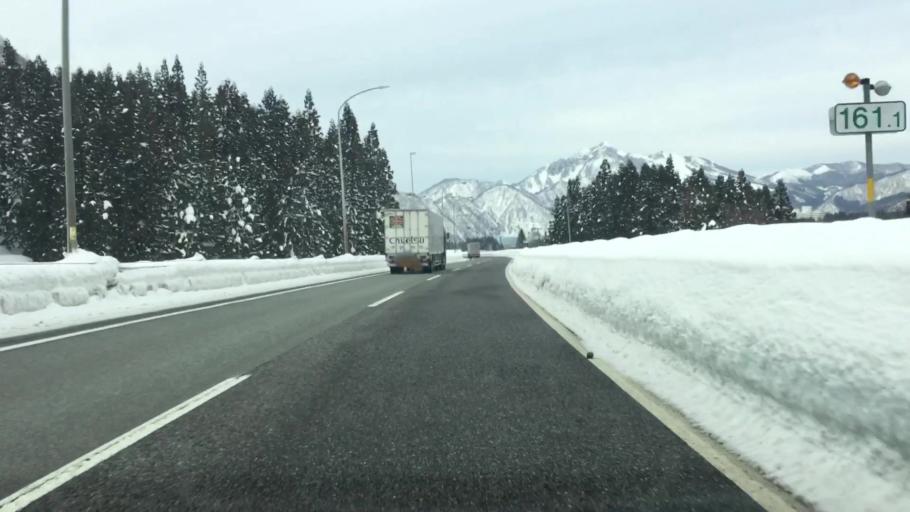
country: JP
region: Niigata
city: Shiozawa
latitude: 36.8885
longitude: 138.8485
